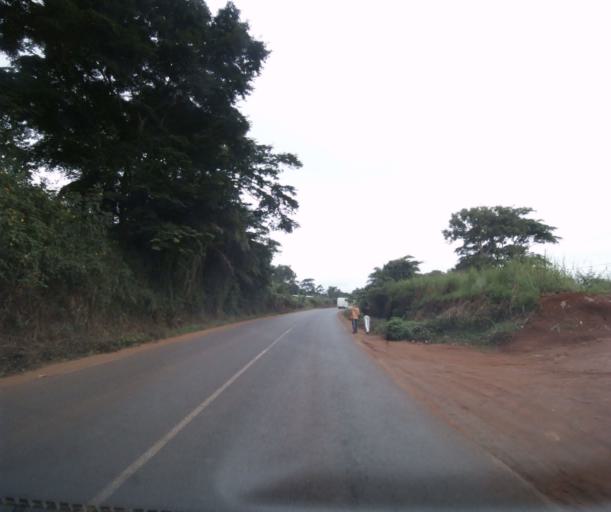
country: CM
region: Centre
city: Mbankomo
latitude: 3.7873
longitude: 11.4292
